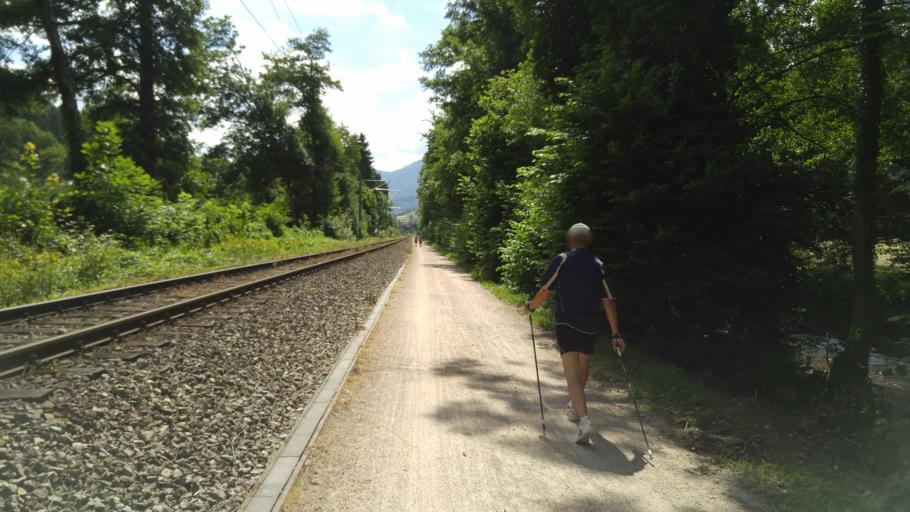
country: DE
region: Baden-Wuerttemberg
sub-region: Freiburg Region
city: Muenstertal/Schwarzwald
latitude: 47.8661
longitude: 7.7505
